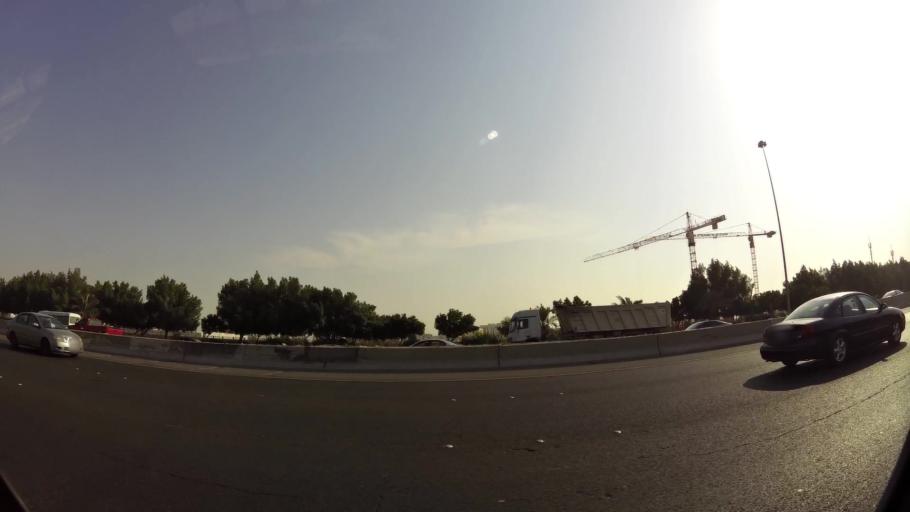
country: KW
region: Al Ahmadi
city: Ar Riqqah
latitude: 29.1337
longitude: 48.0902
